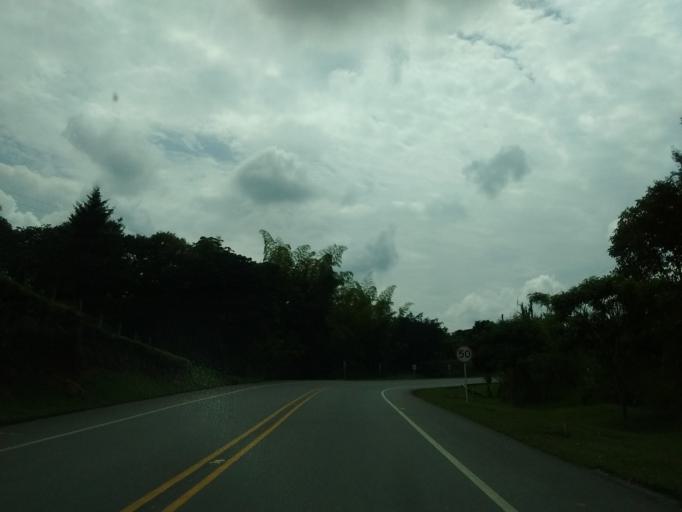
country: CO
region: Cauca
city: Morales
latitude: 2.7125
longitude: -76.5391
